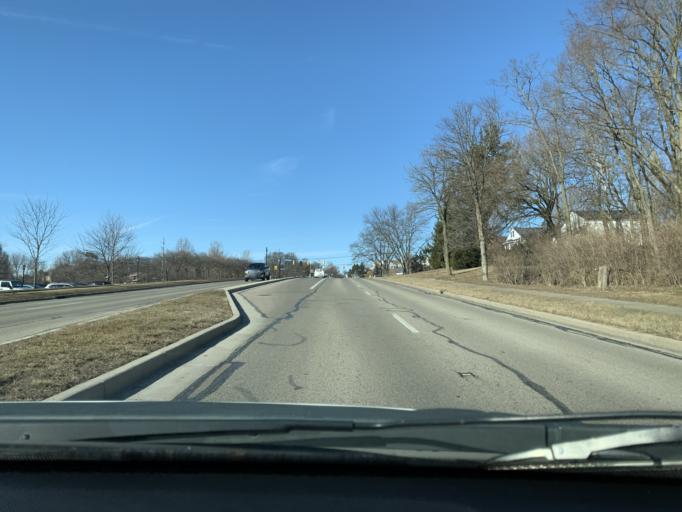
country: US
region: Ohio
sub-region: Montgomery County
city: Centerville
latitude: 39.6421
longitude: -84.1382
